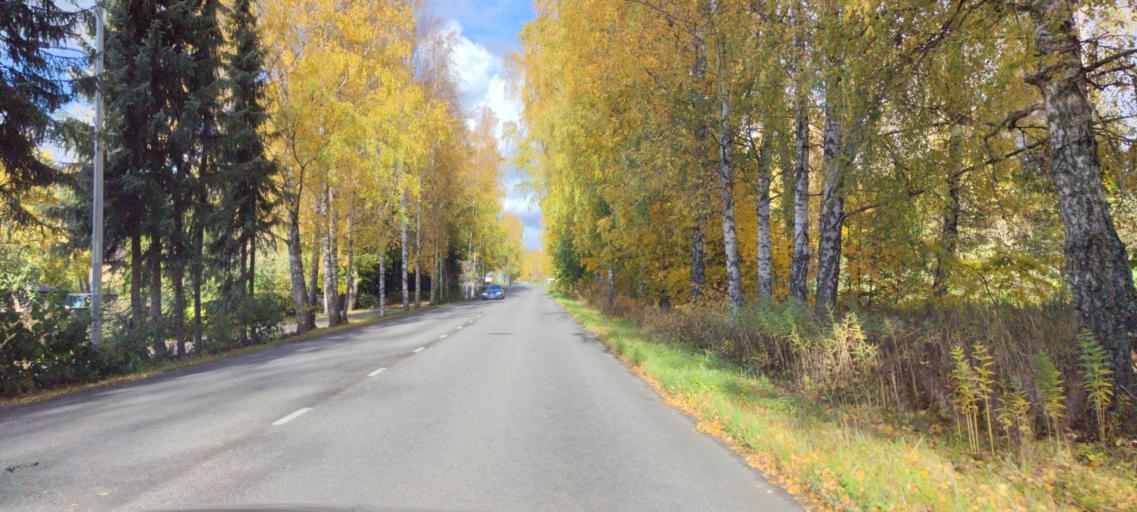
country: FI
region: Varsinais-Suomi
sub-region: Turku
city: Turku
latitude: 60.4199
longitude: 22.2698
